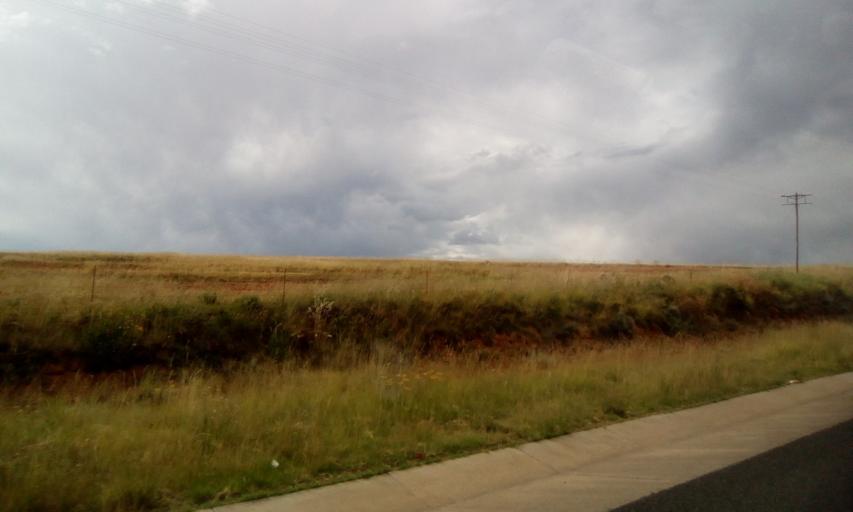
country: ZA
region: Orange Free State
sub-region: Thabo Mofutsanyana District Municipality
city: Ladybrand
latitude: -29.2244
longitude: 27.4531
